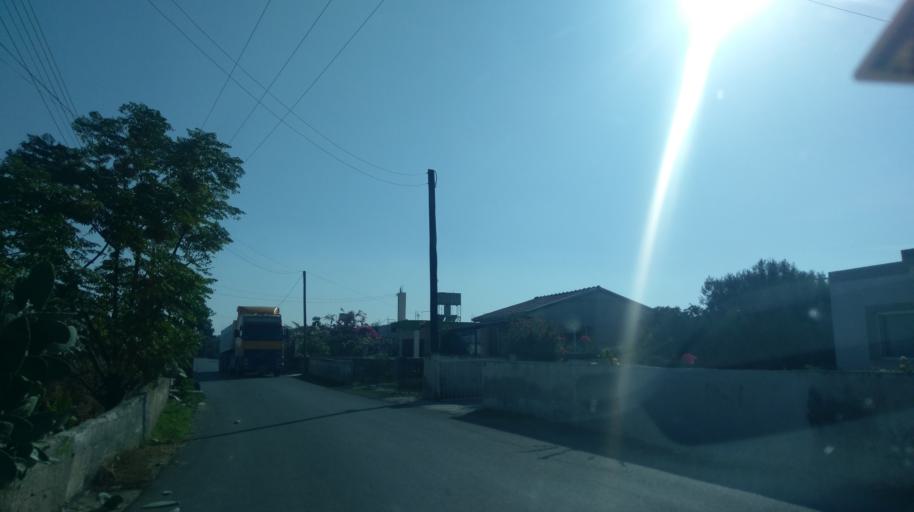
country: CY
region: Larnaka
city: Athienou
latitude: 35.1079
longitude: 33.5648
